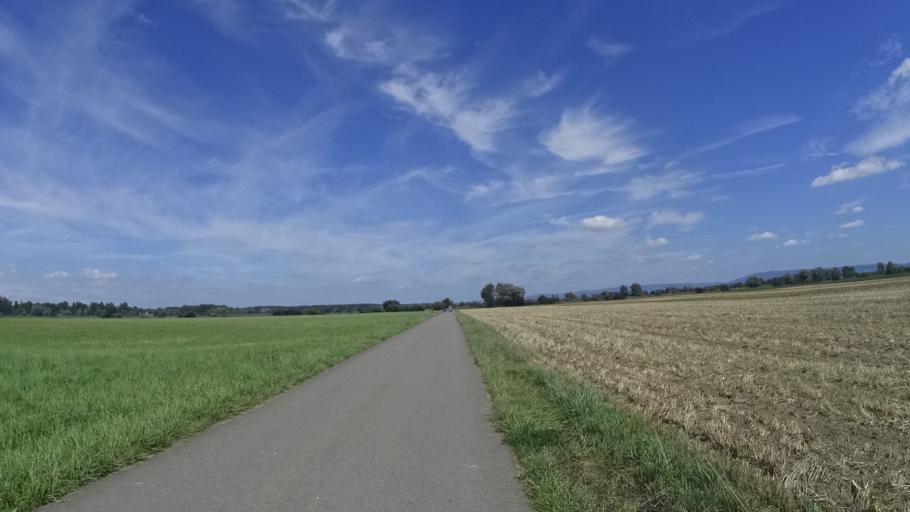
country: DE
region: Baden-Wuerttemberg
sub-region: Karlsruhe Region
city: Altlussheim
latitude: 49.3372
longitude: 8.4886
